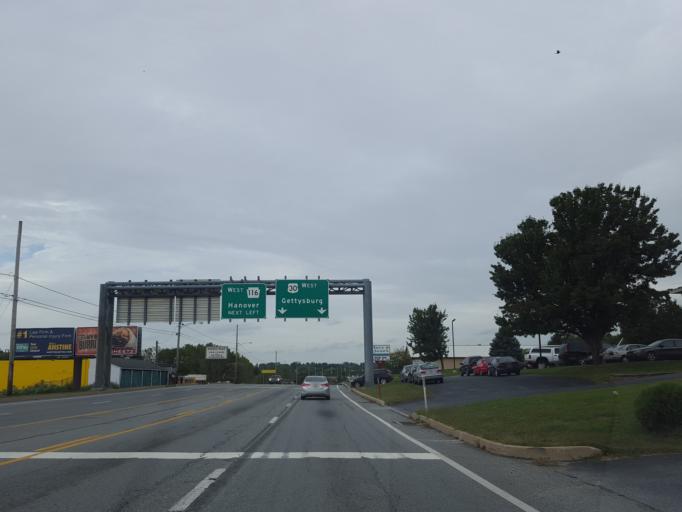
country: US
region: Pennsylvania
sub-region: York County
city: Shiloh
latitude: 39.9300
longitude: -76.8170
